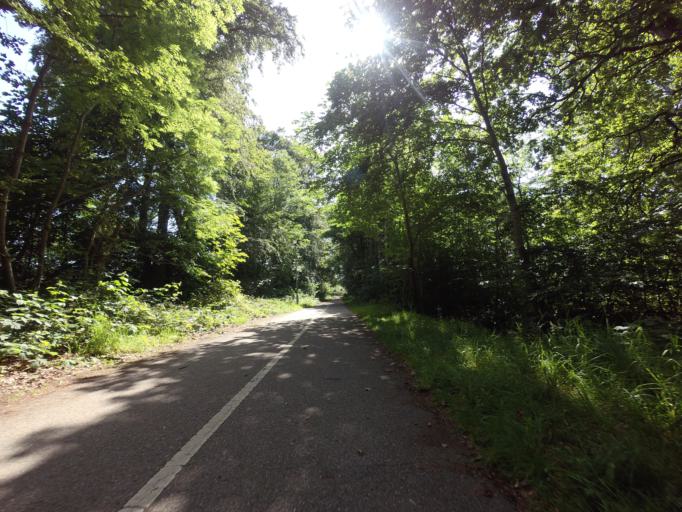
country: GB
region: Scotland
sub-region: Highland
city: Inverness
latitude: 57.4854
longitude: -4.1420
